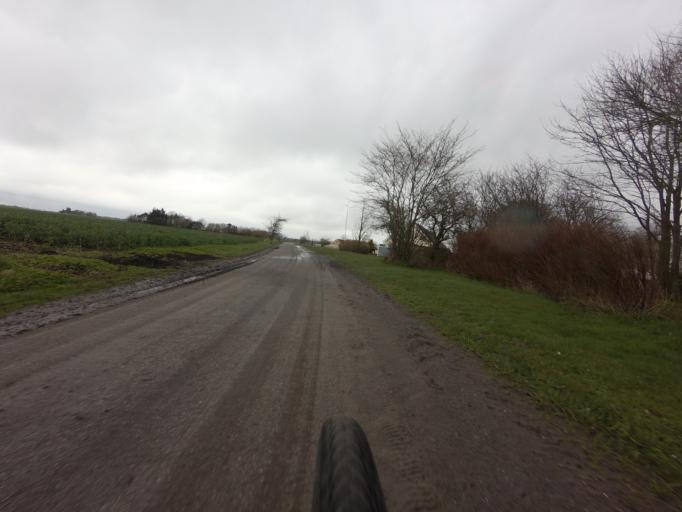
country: DK
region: North Denmark
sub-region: Bronderslev Kommune
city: Bronderslev
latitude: 57.3209
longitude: 9.8061
